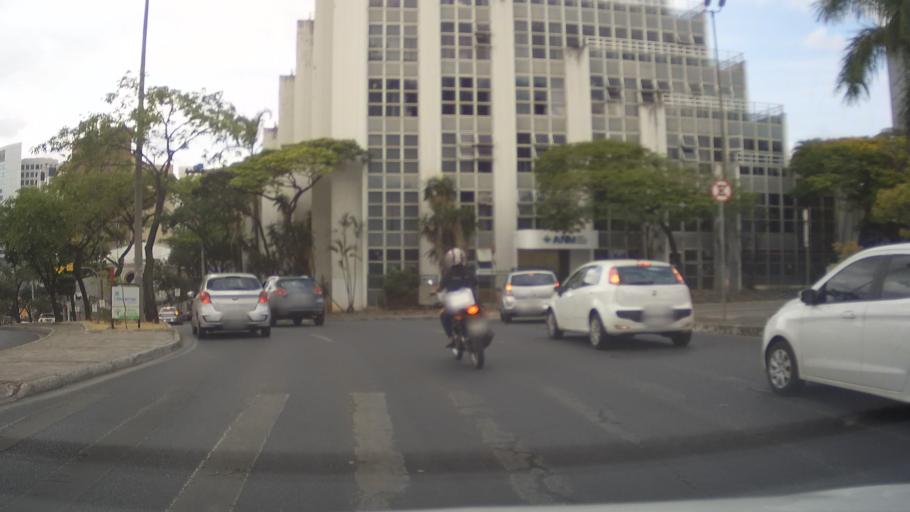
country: BR
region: Minas Gerais
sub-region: Belo Horizonte
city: Belo Horizonte
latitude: -19.9387
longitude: -43.9261
